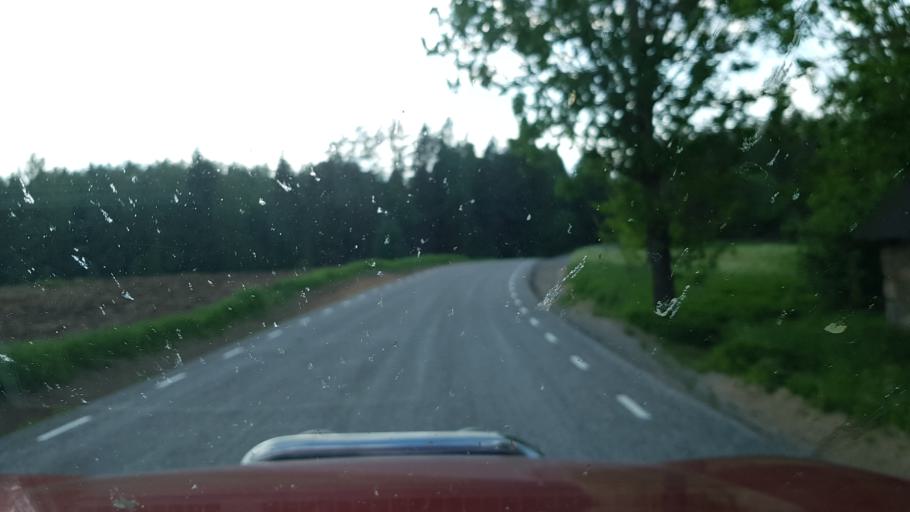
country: EE
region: Tartu
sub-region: UElenurme vald
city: Ulenurme
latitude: 58.1028
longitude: 26.7762
